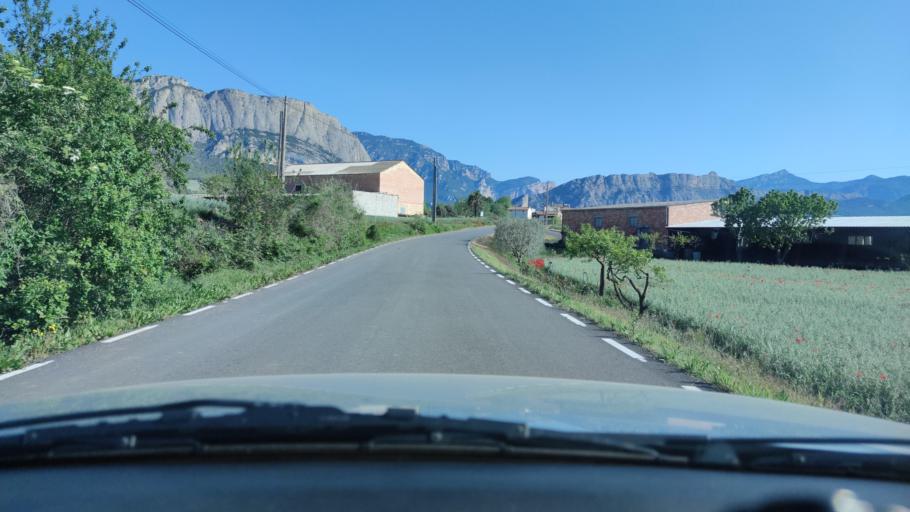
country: ES
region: Catalonia
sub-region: Provincia de Lleida
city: Oliana
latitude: 42.0582
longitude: 1.2960
